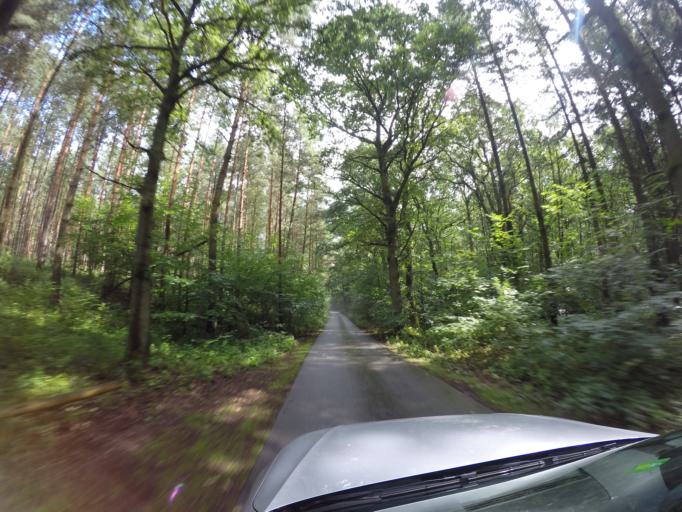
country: DE
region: Mecklenburg-Vorpommern
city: Rechlin
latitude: 53.3555
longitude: 12.8513
